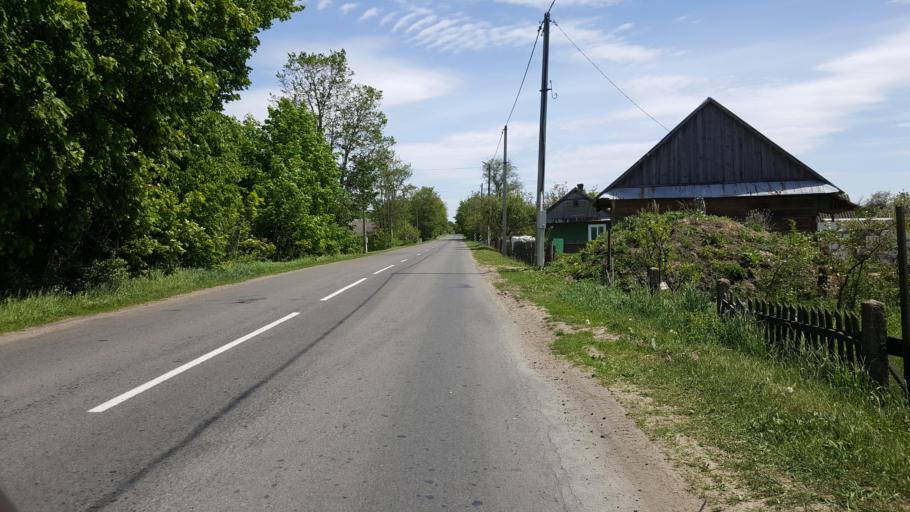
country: BY
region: Brest
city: Kobryn
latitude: 52.3470
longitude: 24.2021
